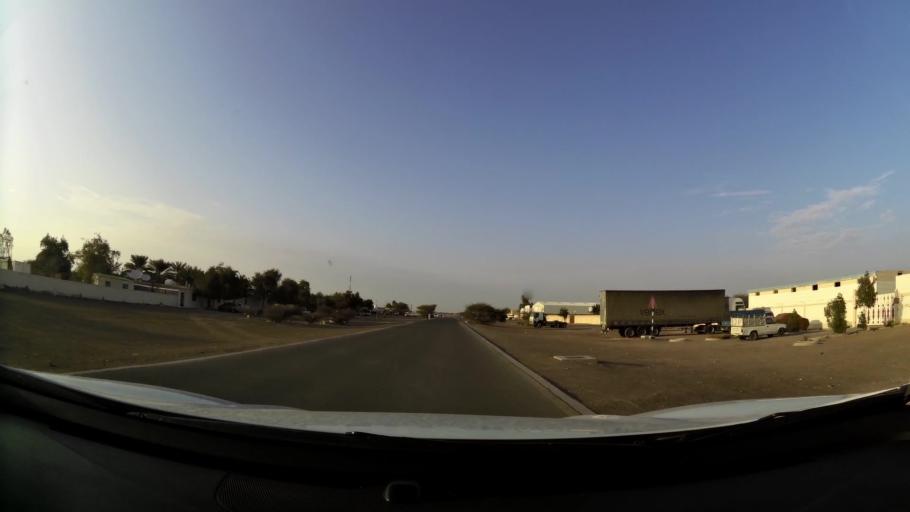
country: AE
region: Abu Dhabi
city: Al Ain
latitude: 24.1555
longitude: 55.8220
